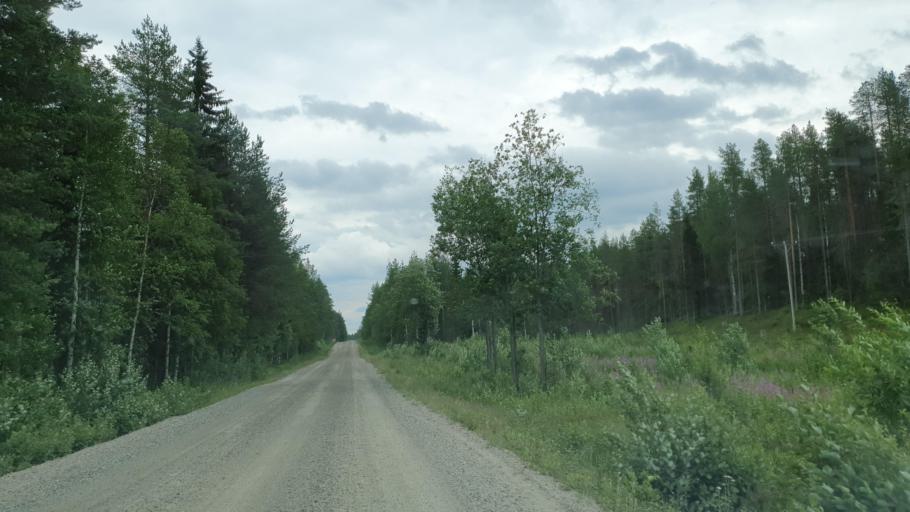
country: RU
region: Republic of Karelia
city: Kostomuksha
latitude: 64.7524
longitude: 29.8911
